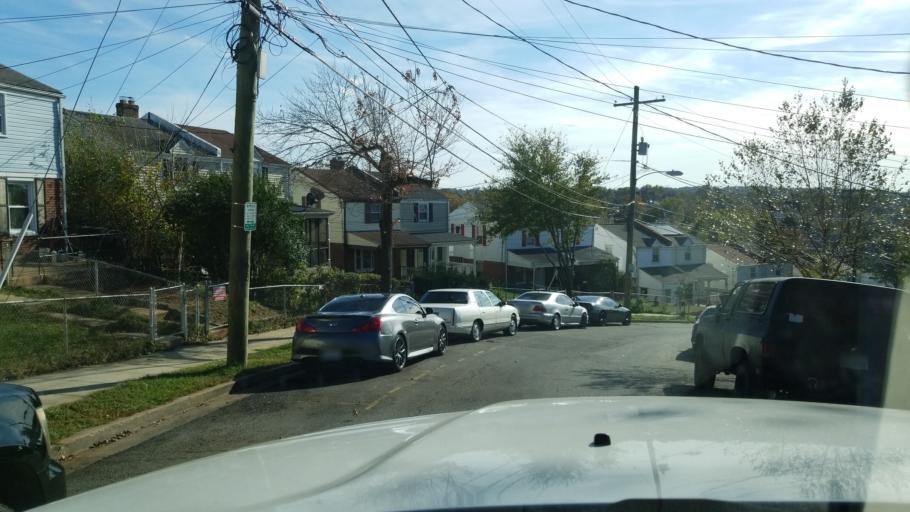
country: US
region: Maryland
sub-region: Prince George's County
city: Fairmount Heights
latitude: 38.9017
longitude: -76.9276
